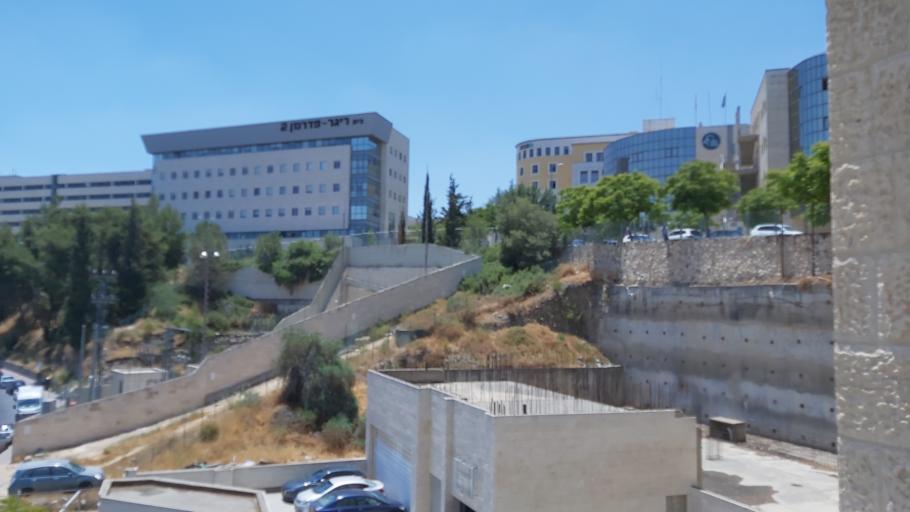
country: PS
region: West Bank
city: Bayt Iksa
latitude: 31.7897
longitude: 35.1870
